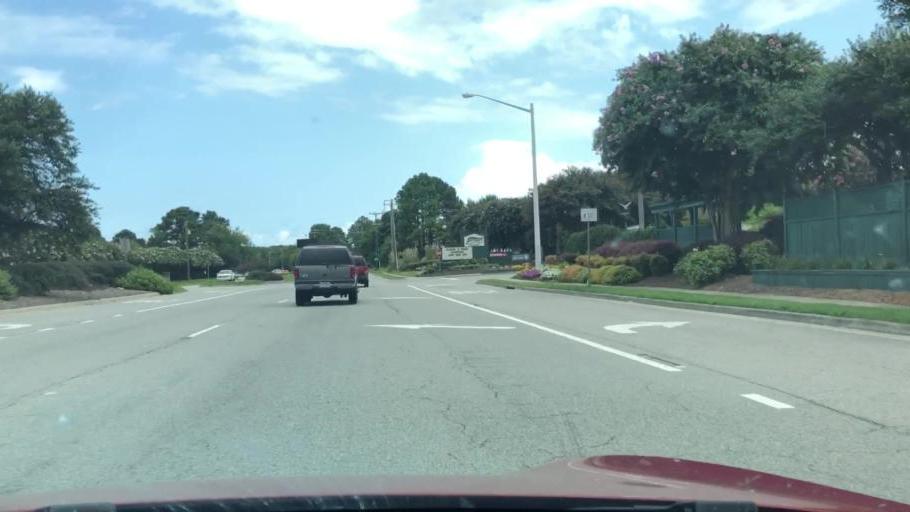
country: US
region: Virginia
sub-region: City of Chesapeake
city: Chesapeake
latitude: 36.8771
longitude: -76.1337
